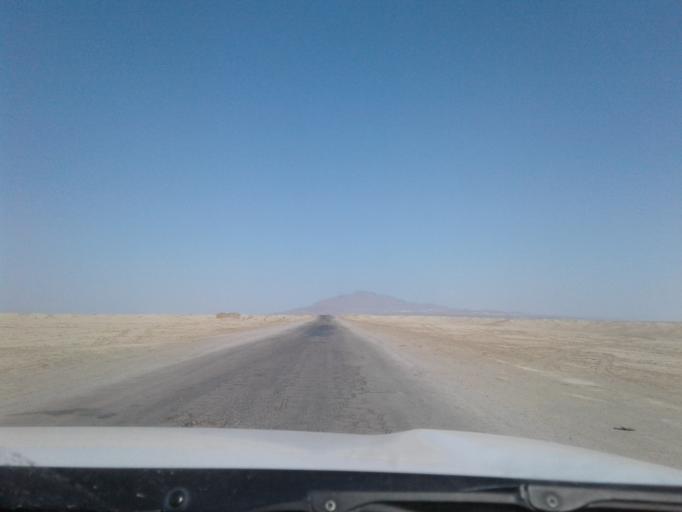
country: TM
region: Balkan
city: Gumdag
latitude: 39.2113
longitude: 54.6347
